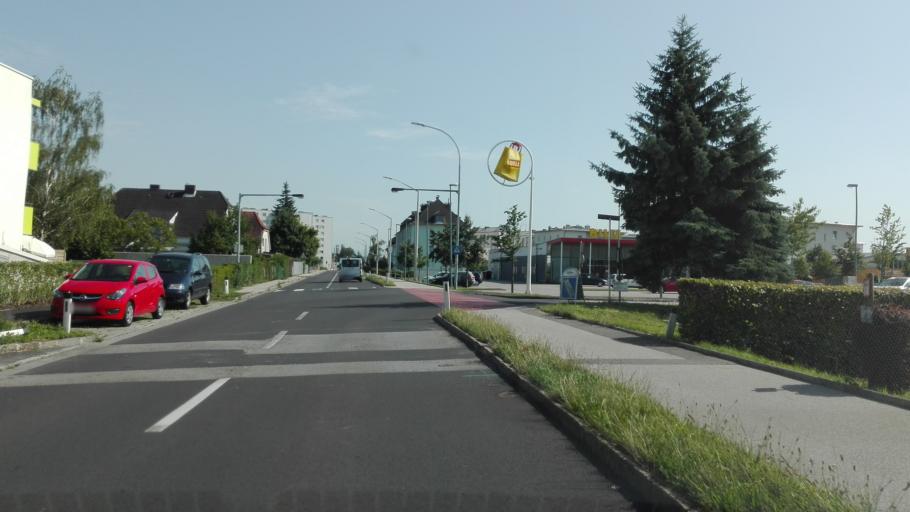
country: AT
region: Upper Austria
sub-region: Politischer Bezirk Linz-Land
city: Leonding
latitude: 48.2483
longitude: 14.2592
